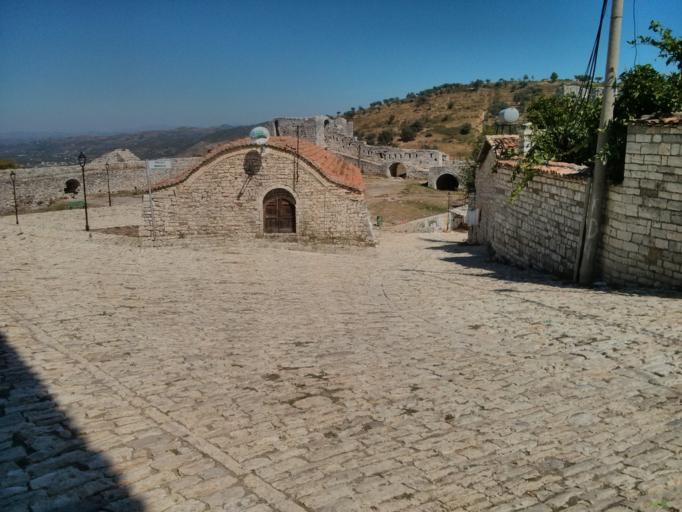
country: AL
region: Berat
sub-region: Rrethi i Beratit
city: Berat
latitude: 40.7098
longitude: 19.9457
